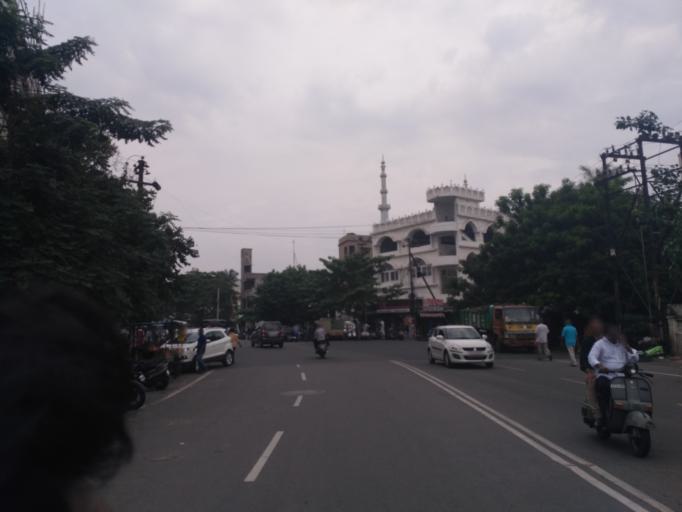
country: IN
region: Andhra Pradesh
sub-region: Vishakhapatnam
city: Yarada
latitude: 17.7229
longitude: 83.3329
